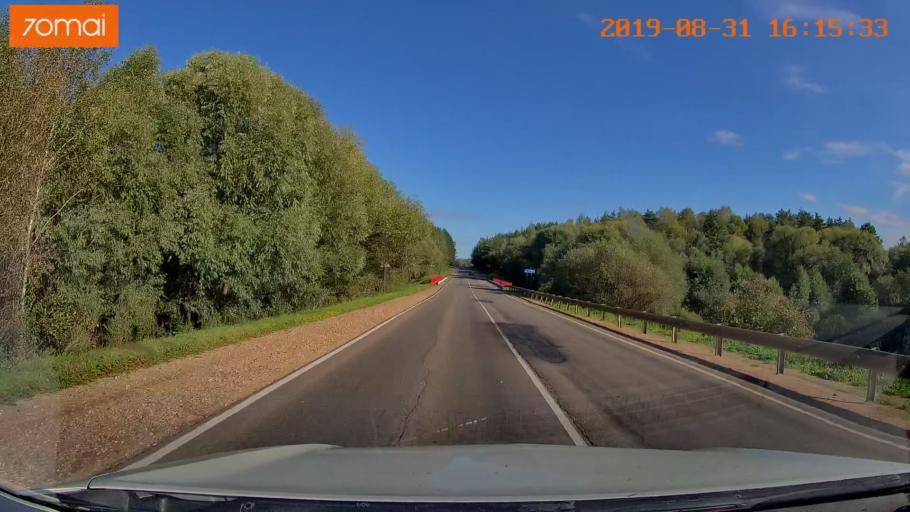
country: RU
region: Kaluga
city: Nikola-Lenivets
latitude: 54.5593
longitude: 35.4893
